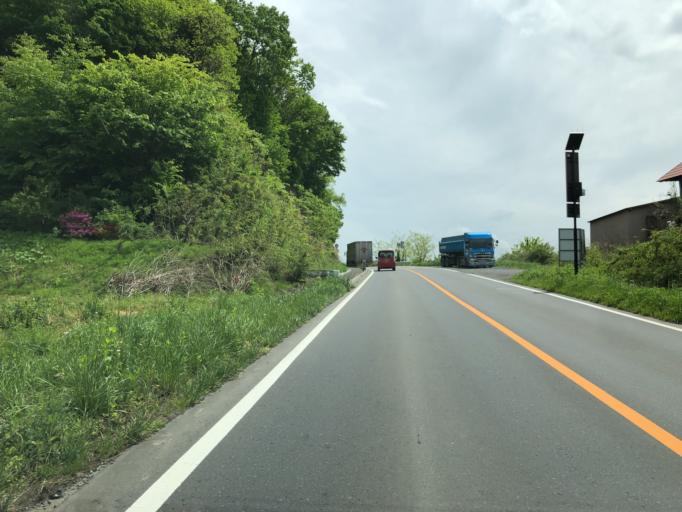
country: JP
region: Fukushima
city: Ishikawa
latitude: 37.0947
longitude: 140.3519
